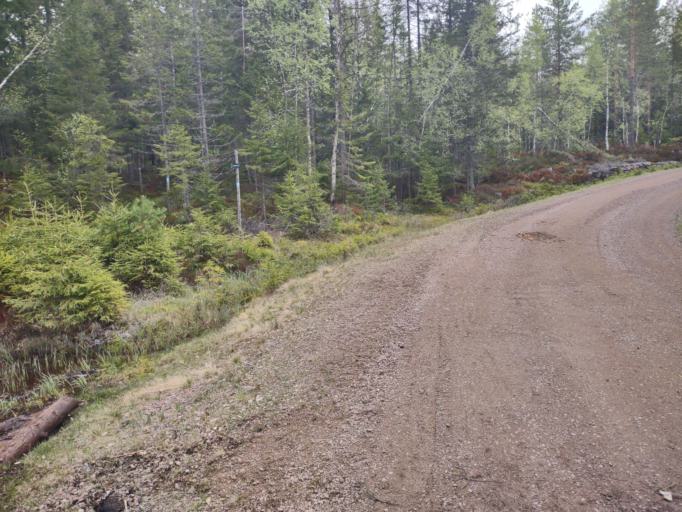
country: NO
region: Oppland
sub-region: Lunner
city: Grua
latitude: 60.3004
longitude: 10.8007
